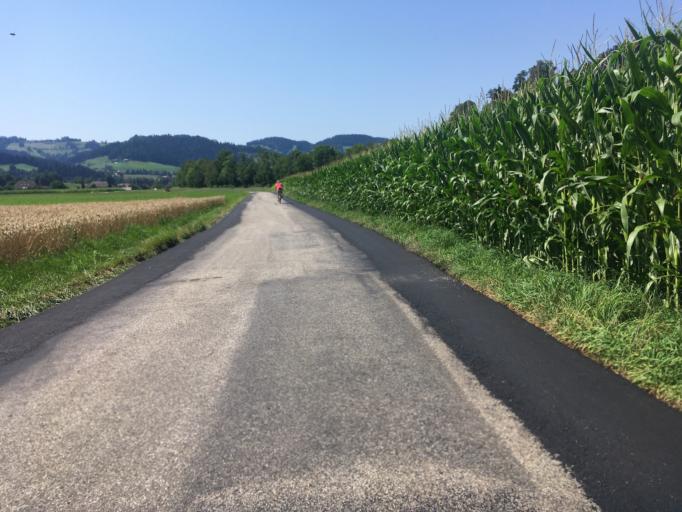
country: CH
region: Bern
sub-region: Emmental District
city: Langnau
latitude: 46.9433
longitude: 7.7712
